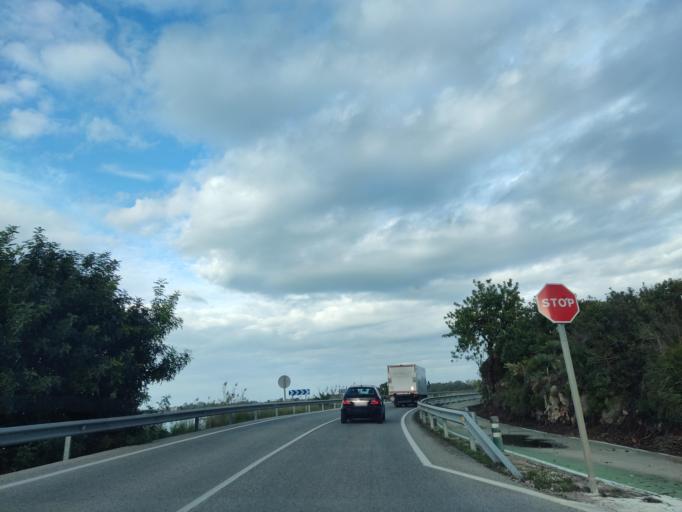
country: ES
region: Valencia
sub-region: Provincia de Alicante
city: Benimeli
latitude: 38.8528
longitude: -0.0333
